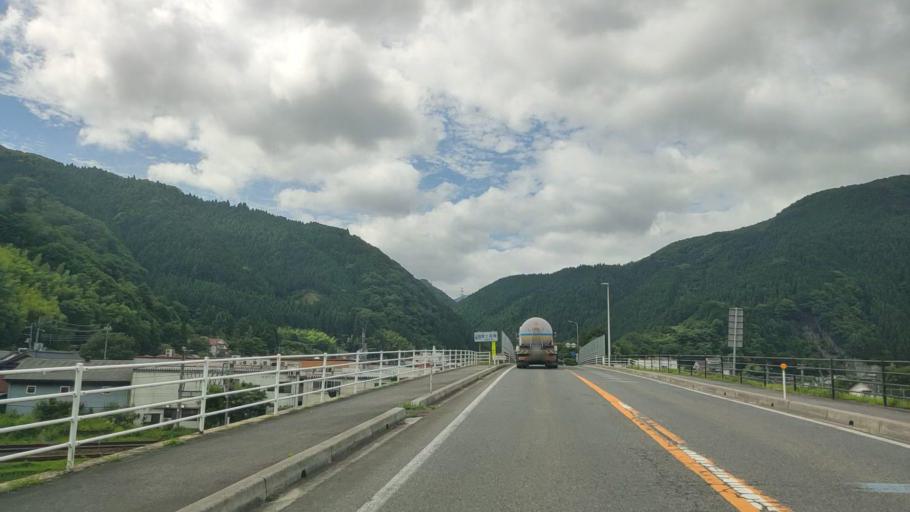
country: JP
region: Tottori
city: Yonago
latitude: 35.2412
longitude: 133.4403
